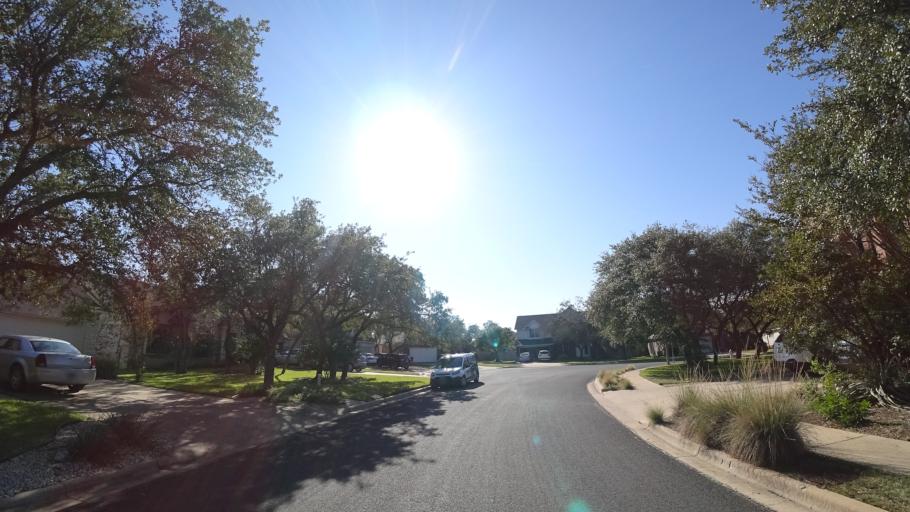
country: US
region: Texas
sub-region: Travis County
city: Shady Hollow
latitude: 30.2049
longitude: -97.8579
